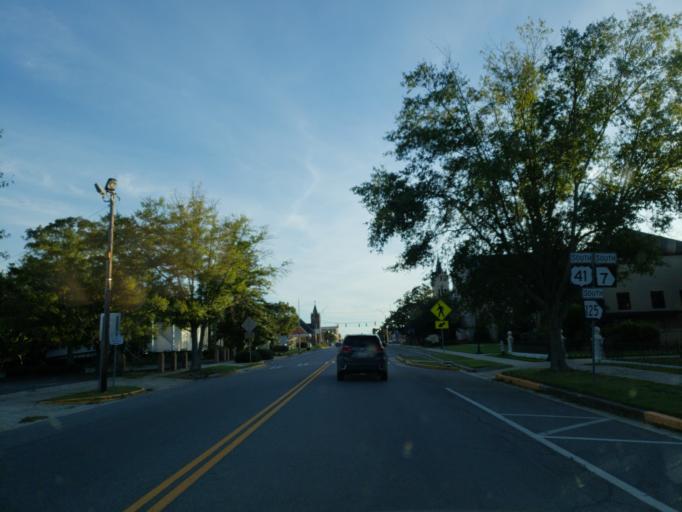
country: US
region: Georgia
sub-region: Tift County
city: Tifton
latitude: 31.4576
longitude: -83.5079
